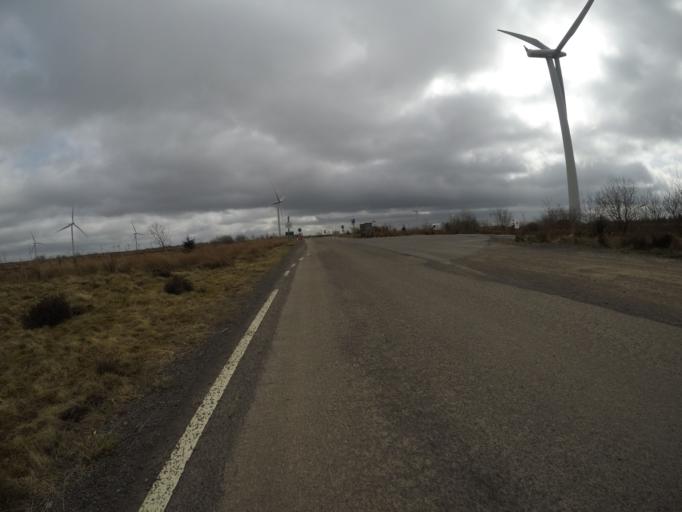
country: GB
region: Scotland
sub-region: East Renfrewshire
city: Newton Mearns
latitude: 55.7038
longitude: -4.3563
